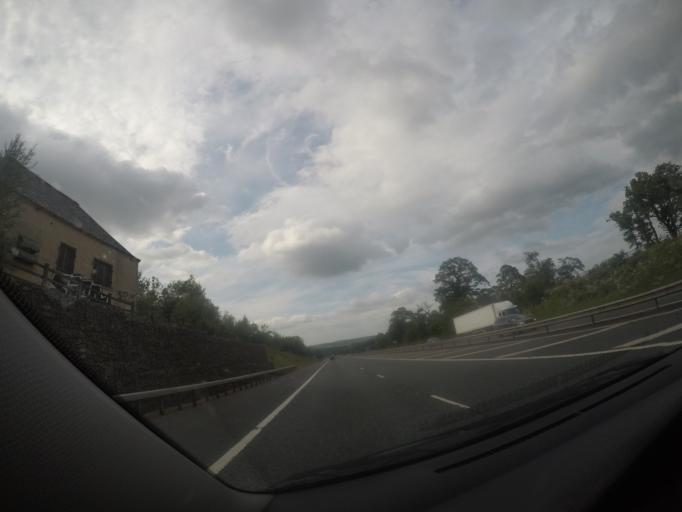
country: GB
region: Scotland
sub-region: South Lanarkshire
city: Douglas
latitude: 55.5658
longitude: -3.8066
